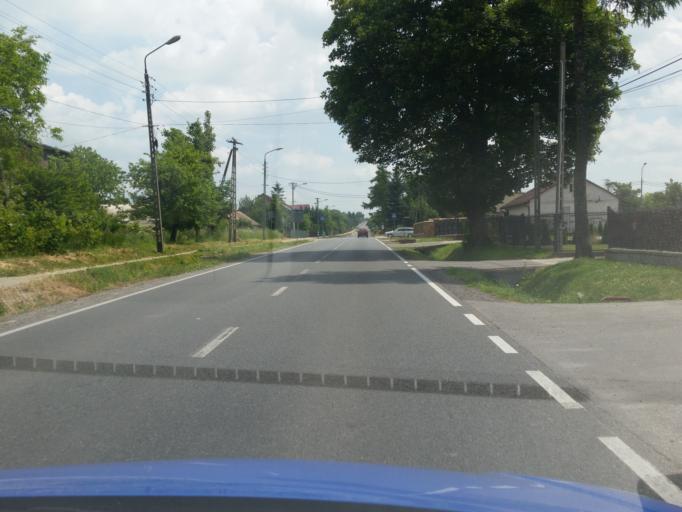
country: PL
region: Lesser Poland Voivodeship
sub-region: Powiat miechowski
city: Miechow
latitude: 50.3573
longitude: 20.0618
